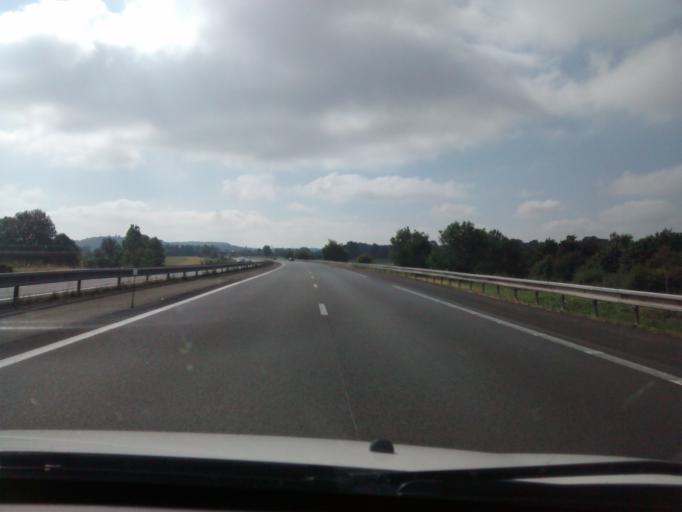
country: FR
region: Pays de la Loire
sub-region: Departement de la Sarthe
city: Brulon
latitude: 48.0108
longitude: -0.2949
